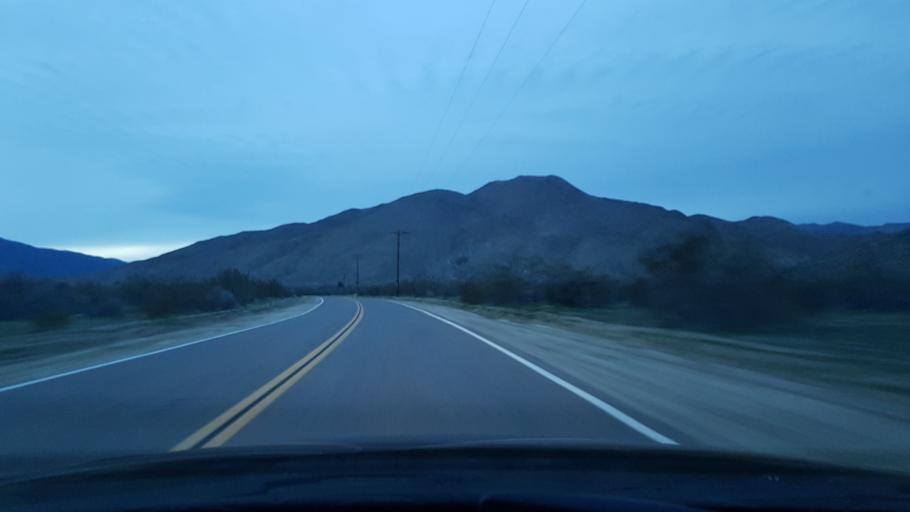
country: US
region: California
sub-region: San Diego County
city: Julian
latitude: 33.0873
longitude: -116.4491
